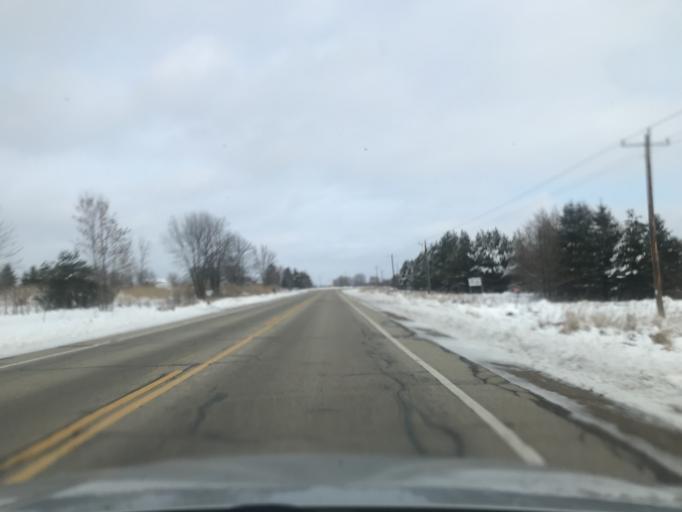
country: US
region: Wisconsin
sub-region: Oconto County
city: Oconto
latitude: 44.8915
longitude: -88.0027
